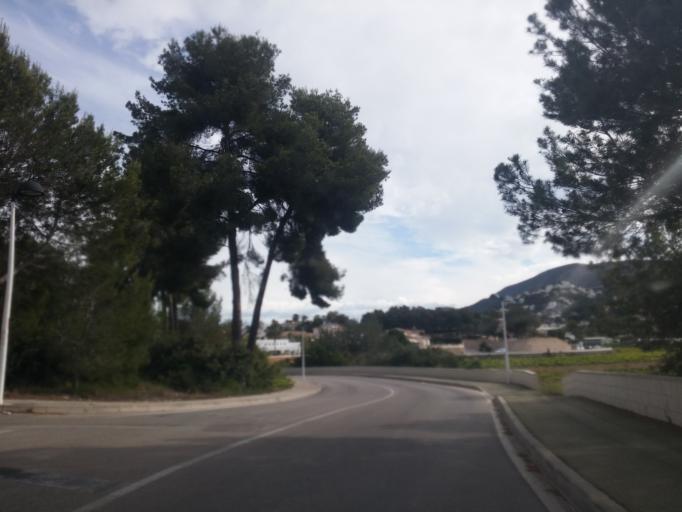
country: ES
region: Valencia
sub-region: Provincia de Alicante
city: Moraira
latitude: 38.7007
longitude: 0.1314
